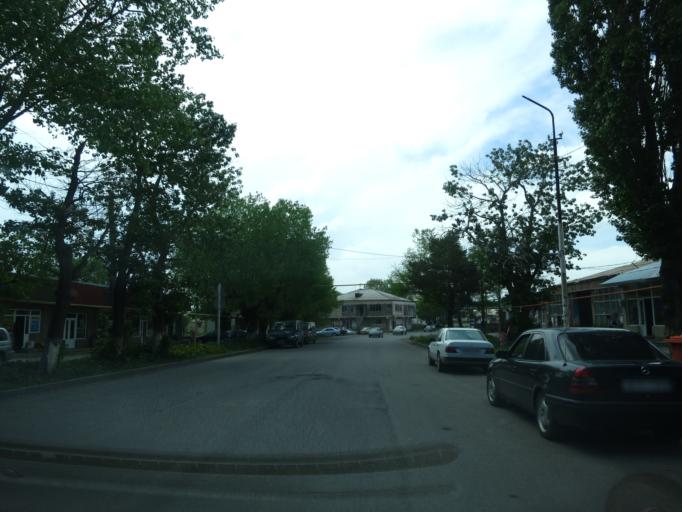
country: GE
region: Samtskhe-Javakheti
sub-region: Ninotsminda
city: Ninotsminda
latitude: 41.2673
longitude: 43.5888
